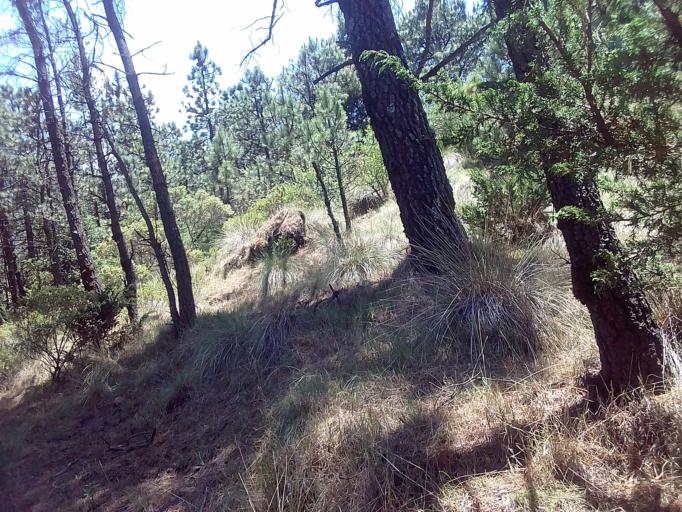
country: MX
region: Mexico City
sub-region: Cuajimalpa de Morelos
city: San Lorenzo Acopilco
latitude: 19.2869
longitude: -99.3347
